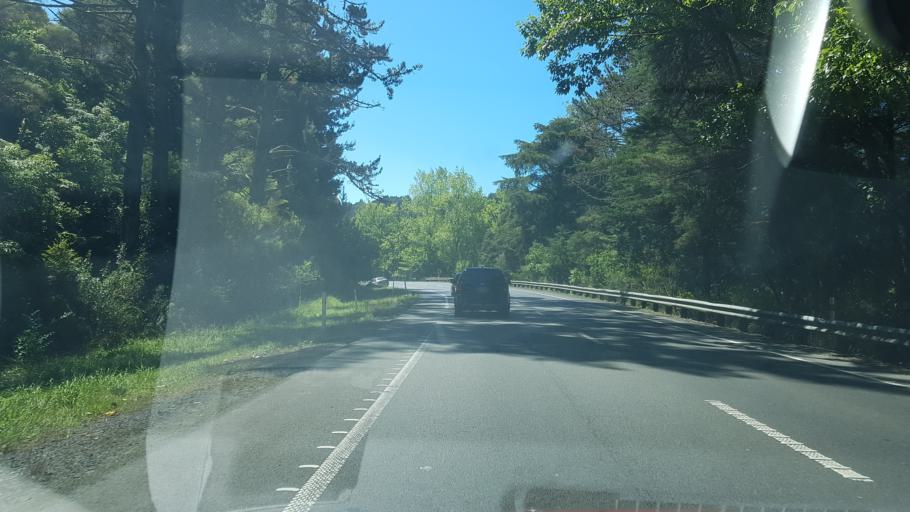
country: NZ
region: Auckland
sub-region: Auckland
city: Warkworth
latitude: -36.4450
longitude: 174.6503
